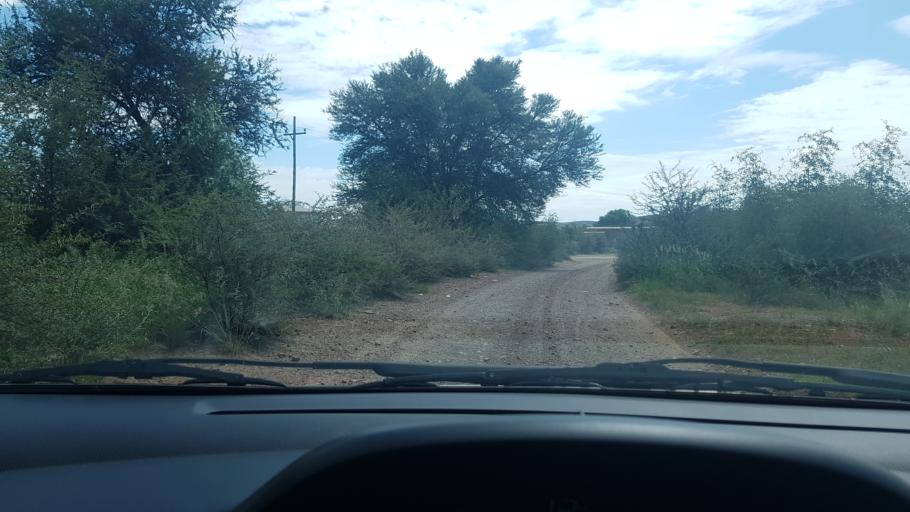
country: ZA
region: Northern Cape
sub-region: Siyanda District Municipality
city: Danielskuil
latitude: -28.1922
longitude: 23.5455
